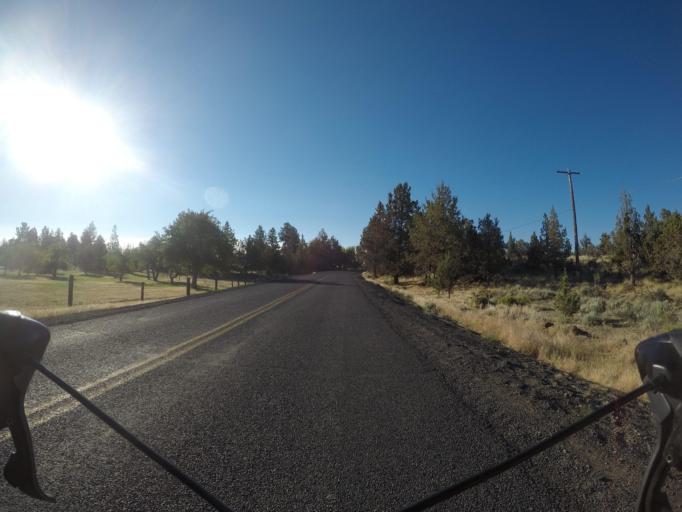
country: US
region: Oregon
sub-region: Deschutes County
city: Redmond
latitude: 44.2674
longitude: -121.2499
